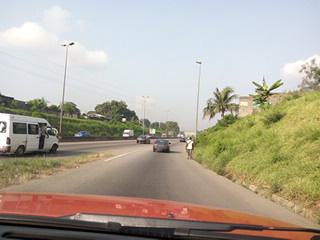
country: CI
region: Lagunes
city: Abidjan
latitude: 5.3545
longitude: -3.9924
